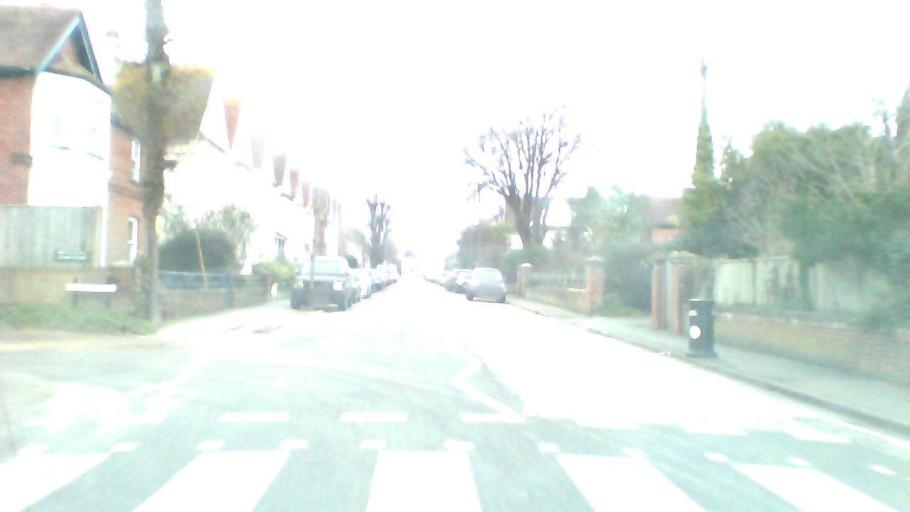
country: GB
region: England
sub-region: Isle of Wight
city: Bembridge
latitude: 50.6888
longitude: -1.0868
